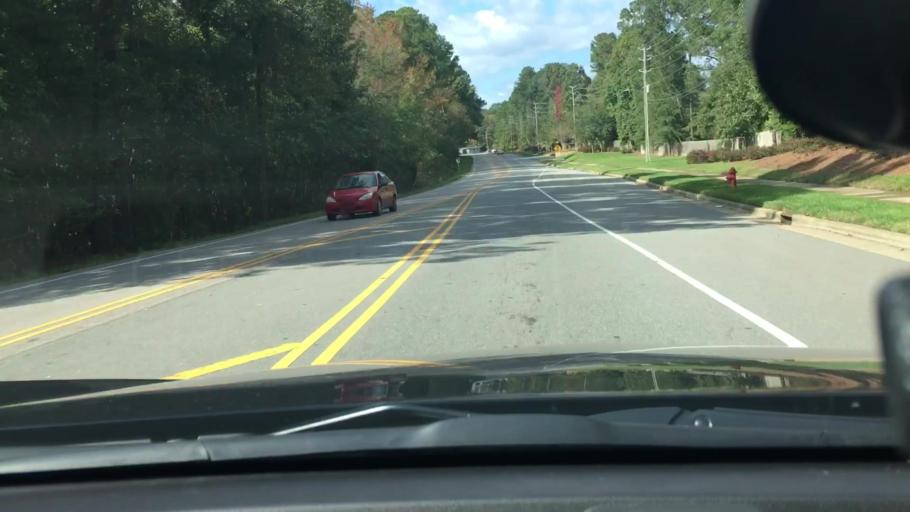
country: US
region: North Carolina
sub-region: Wake County
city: Holly Springs
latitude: 35.6817
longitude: -78.8297
